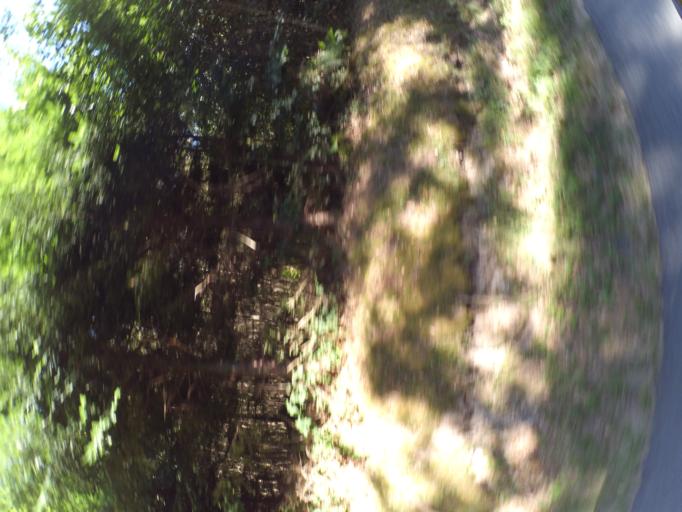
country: FR
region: Limousin
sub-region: Departement de la Haute-Vienne
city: Peyrat-le-Chateau
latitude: 45.7837
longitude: 1.8592
